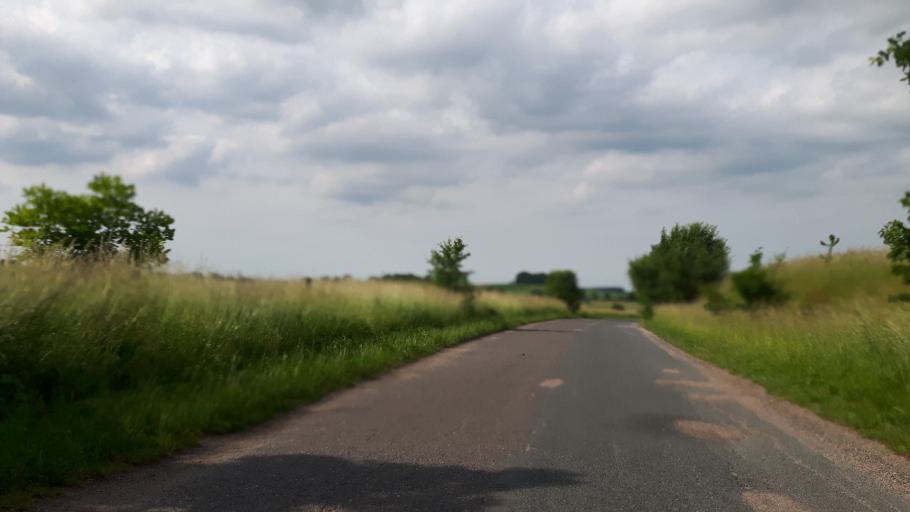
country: PL
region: West Pomeranian Voivodeship
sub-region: Powiat gryficki
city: Gryfice
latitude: 53.8183
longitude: 15.1327
